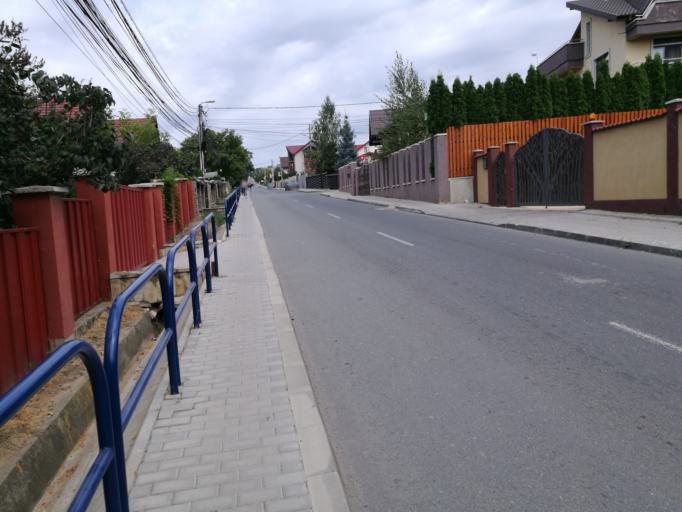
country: RO
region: Iasi
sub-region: Comuna Valea Lupului
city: Valea Lupului
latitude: 47.1754
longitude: 27.5194
